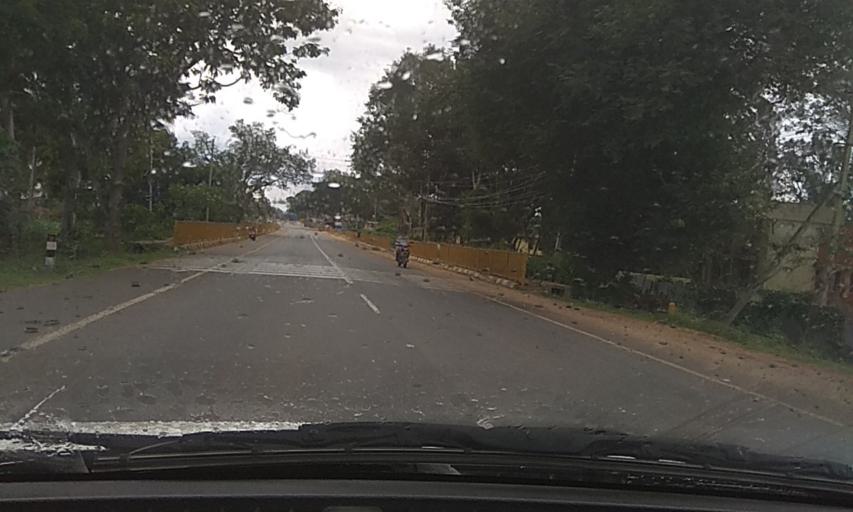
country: IN
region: Karnataka
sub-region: Tumkur
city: Kunigal
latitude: 12.9395
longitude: 77.0285
